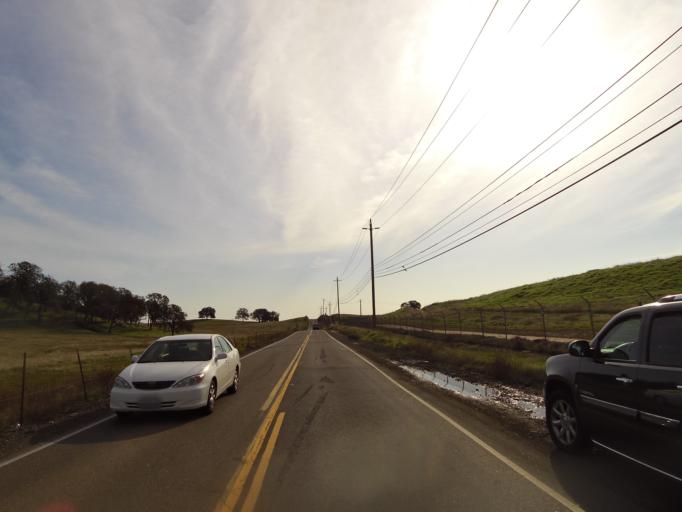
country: US
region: California
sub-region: Sacramento County
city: Folsom
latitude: 38.6324
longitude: -121.1503
